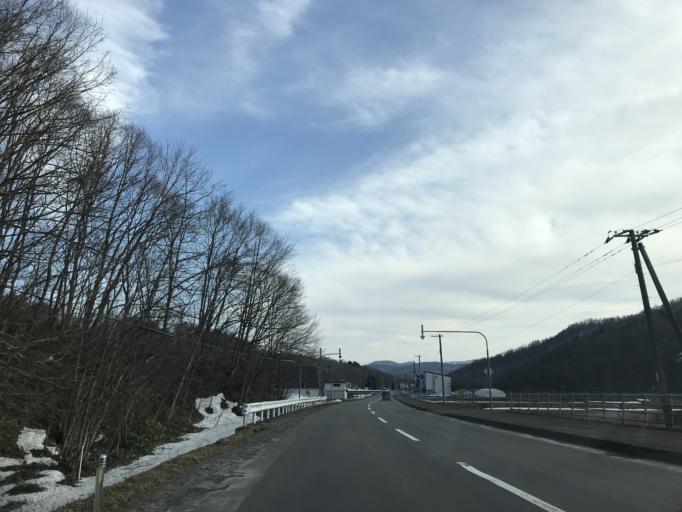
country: JP
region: Hokkaido
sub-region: Asahikawa-shi
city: Asahikawa
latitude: 43.7299
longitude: 142.3208
